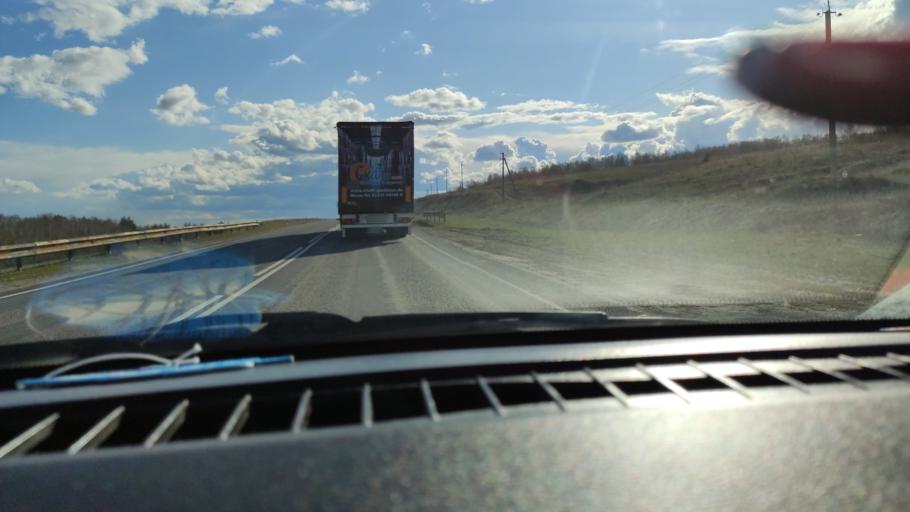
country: RU
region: Saratov
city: Sinodskoye
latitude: 52.0711
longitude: 46.7783
